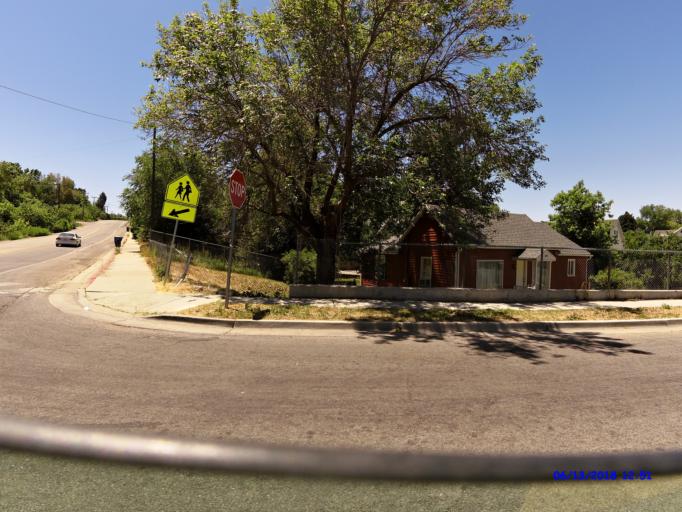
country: US
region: Utah
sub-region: Weber County
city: South Ogden
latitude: 41.2077
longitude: -111.9568
